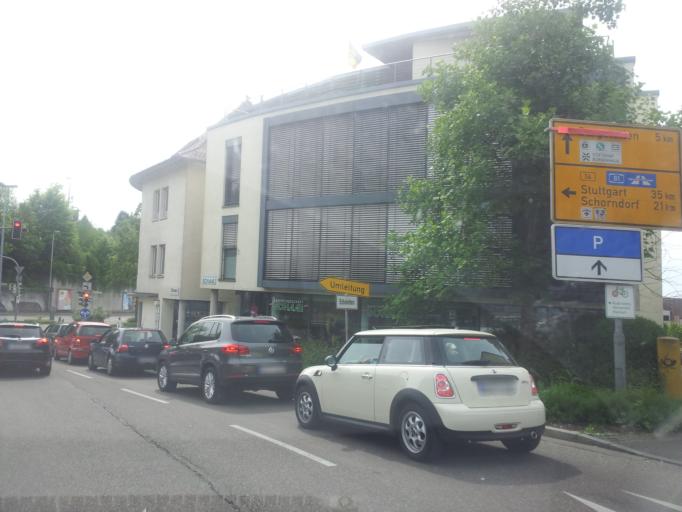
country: DE
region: Baden-Wuerttemberg
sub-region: Regierungsbezirk Stuttgart
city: Backnang
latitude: 48.9447
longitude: 9.4345
